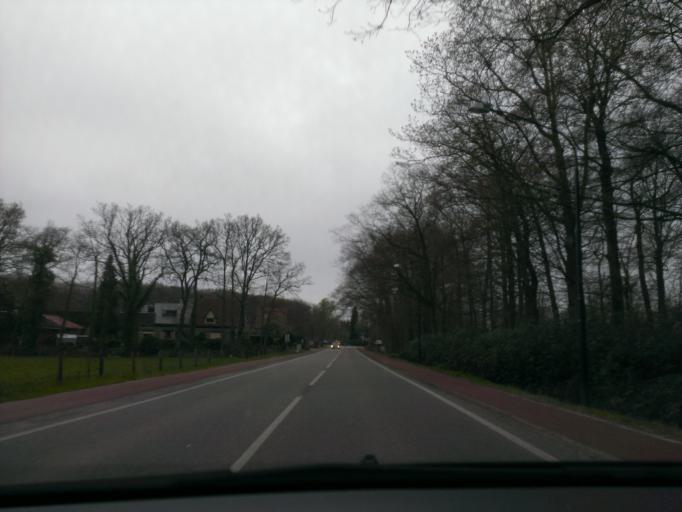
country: NL
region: Gelderland
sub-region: Gemeente Epe
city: Vaassen
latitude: 52.2565
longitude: 5.9518
